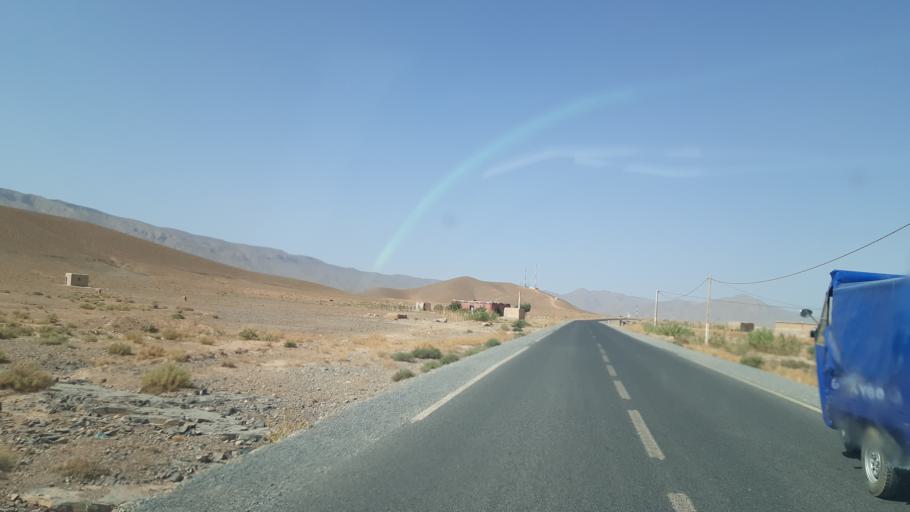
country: MA
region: Meknes-Tafilalet
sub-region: Errachidia
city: Errachidia
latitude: 32.2484
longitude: -4.5824
